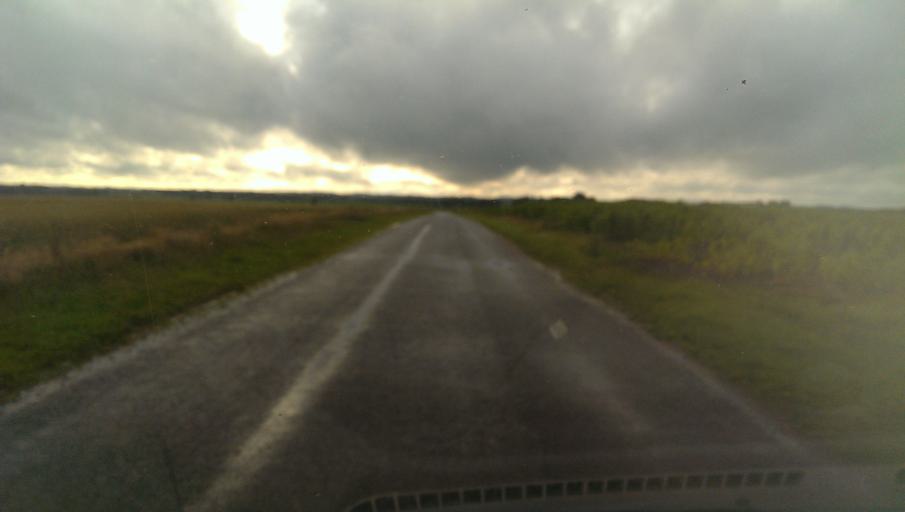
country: DK
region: South Denmark
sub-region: Esbjerg Kommune
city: Bramming
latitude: 55.5005
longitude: 8.6511
